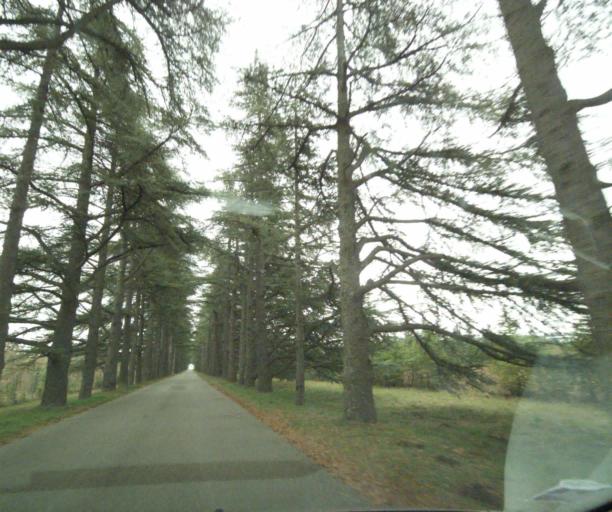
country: FR
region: Provence-Alpes-Cote d'Azur
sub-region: Departement du Var
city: Vinon-sur-Verdon
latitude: 43.7121
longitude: 5.7581
